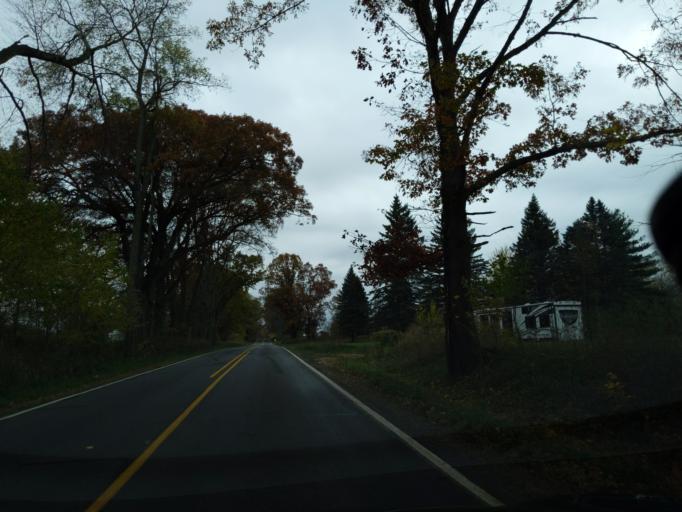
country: US
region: Michigan
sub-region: Jackson County
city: Spring Arbor
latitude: 42.3544
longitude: -84.6005
